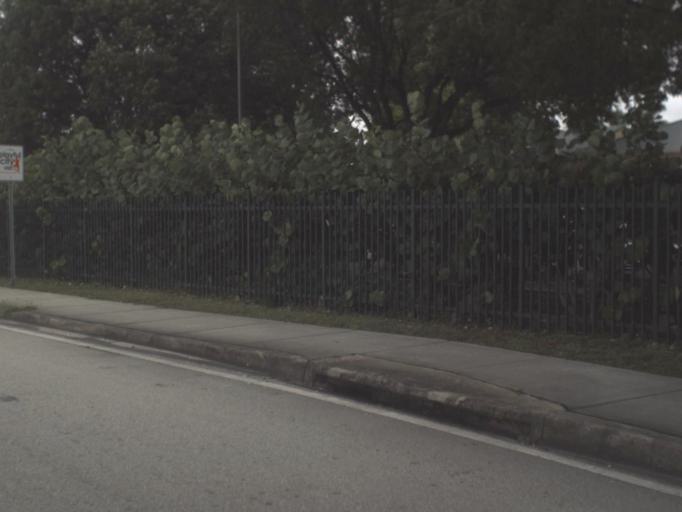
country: US
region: Florida
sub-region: Miami-Dade County
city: Virginia Gardens
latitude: 25.8094
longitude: -80.3238
